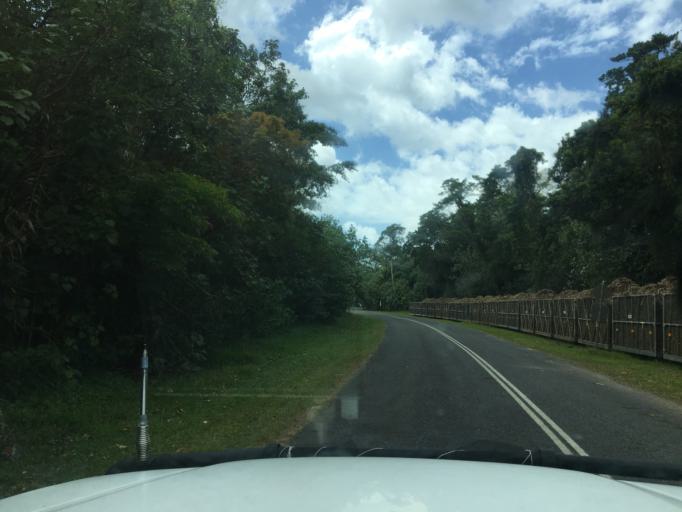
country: AU
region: Queensland
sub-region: Cairns
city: Woree
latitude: -17.2167
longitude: 145.9186
